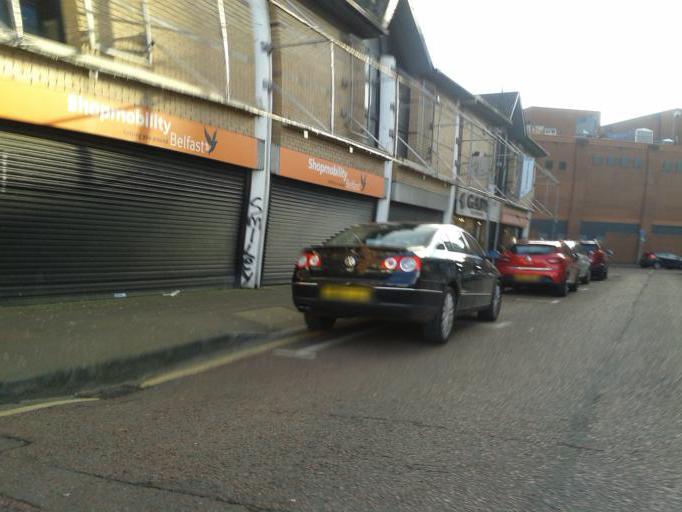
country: GB
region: Northern Ireland
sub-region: City of Belfast
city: Belfast
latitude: 54.6016
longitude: -5.9323
